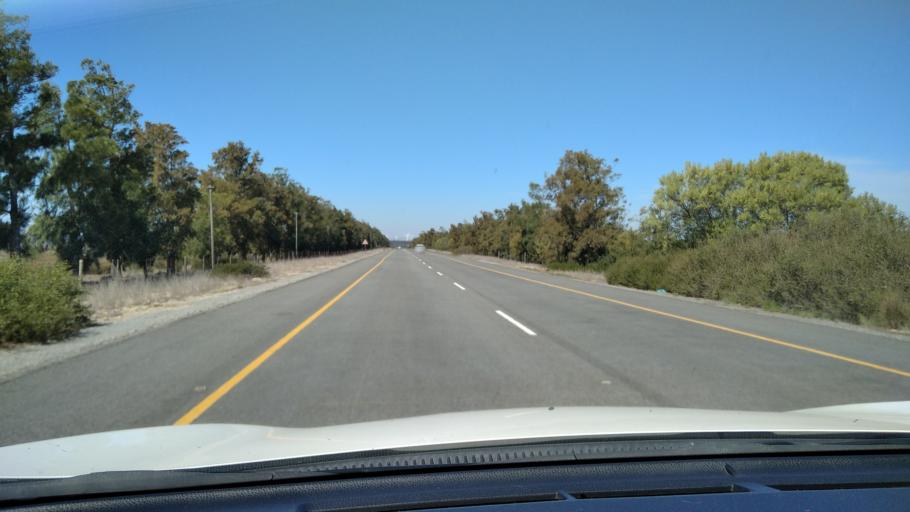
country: ZA
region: Western Cape
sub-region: West Coast District Municipality
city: Vredenburg
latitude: -33.0431
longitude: 18.3153
